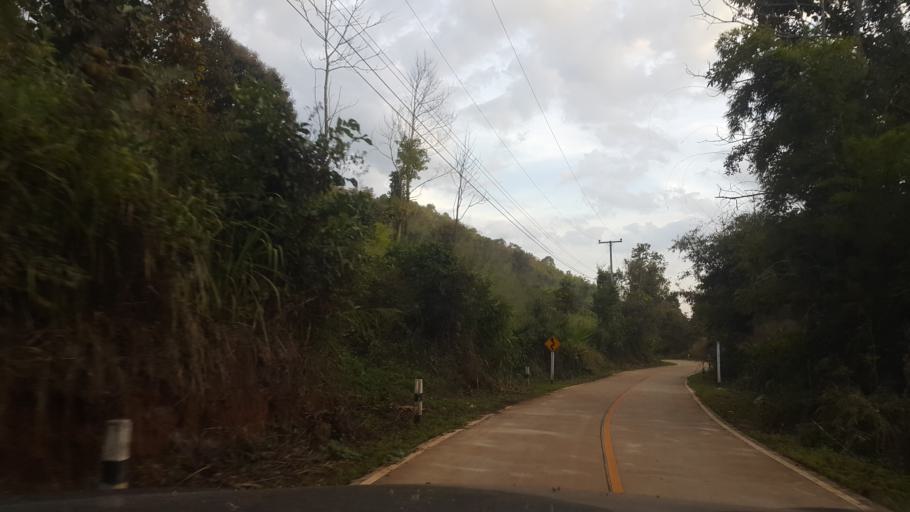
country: TH
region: Chiang Mai
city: Samoeng
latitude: 18.9924
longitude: 98.6749
